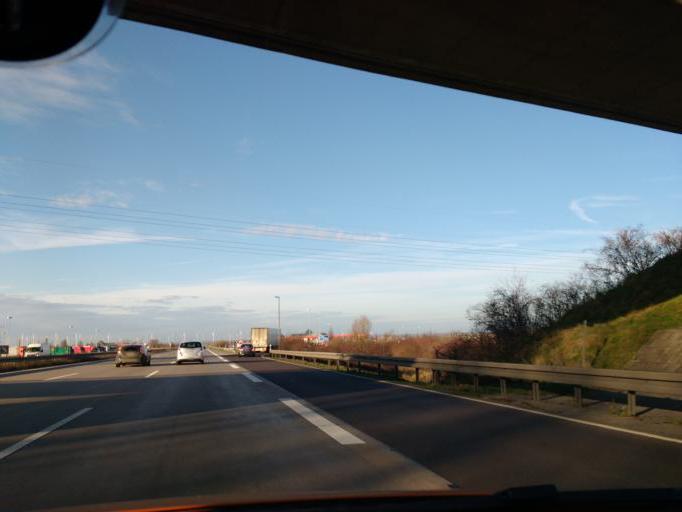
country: DE
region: Saxony-Anhalt
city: Gross Santersleben
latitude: 52.1830
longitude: 11.4575
